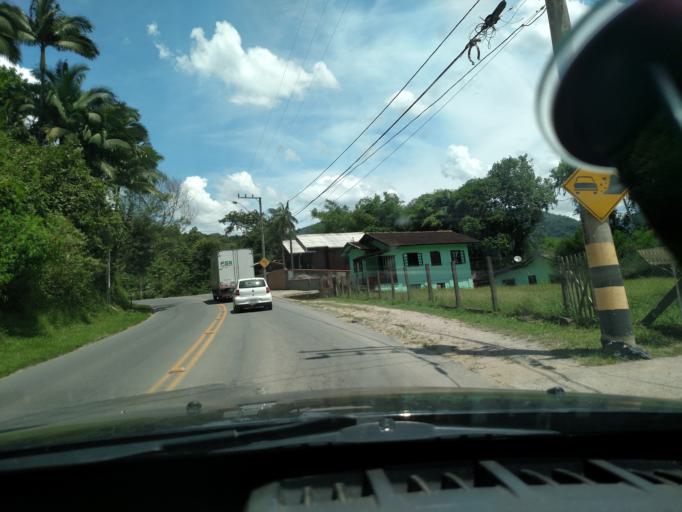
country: BR
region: Santa Catarina
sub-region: Blumenau
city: Blumenau
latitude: -26.9786
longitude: -49.0759
